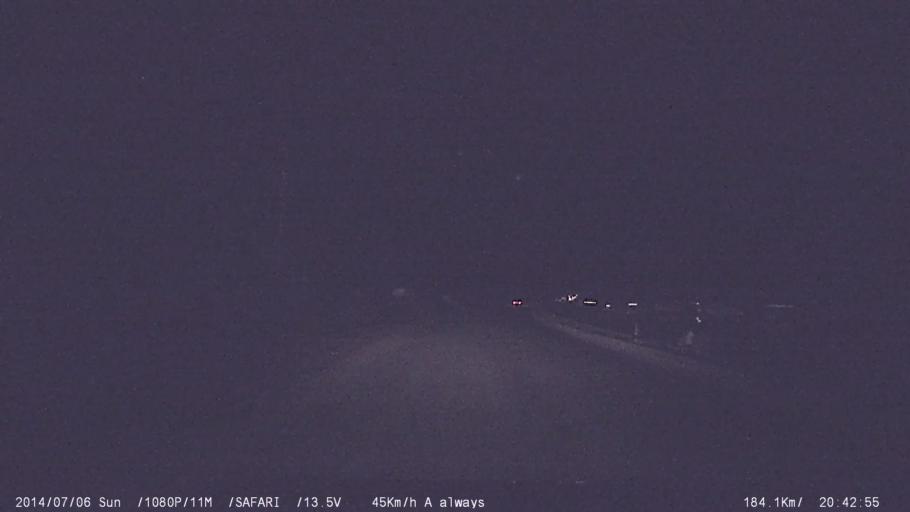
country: IN
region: Tamil Nadu
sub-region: Coimbatore
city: Madukkarai
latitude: 10.8444
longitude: 76.8387
